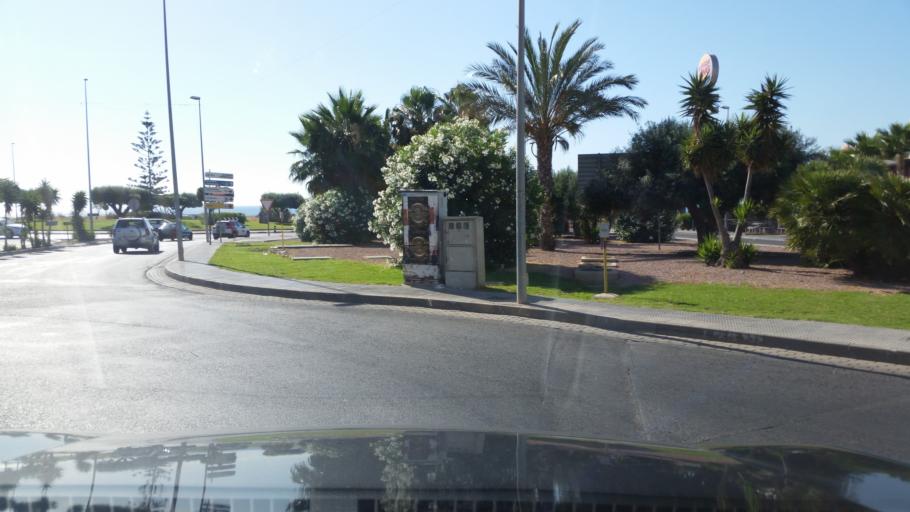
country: ES
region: Valencia
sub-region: Provincia de Alicante
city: Torrevieja
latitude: 37.9377
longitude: -0.7219
